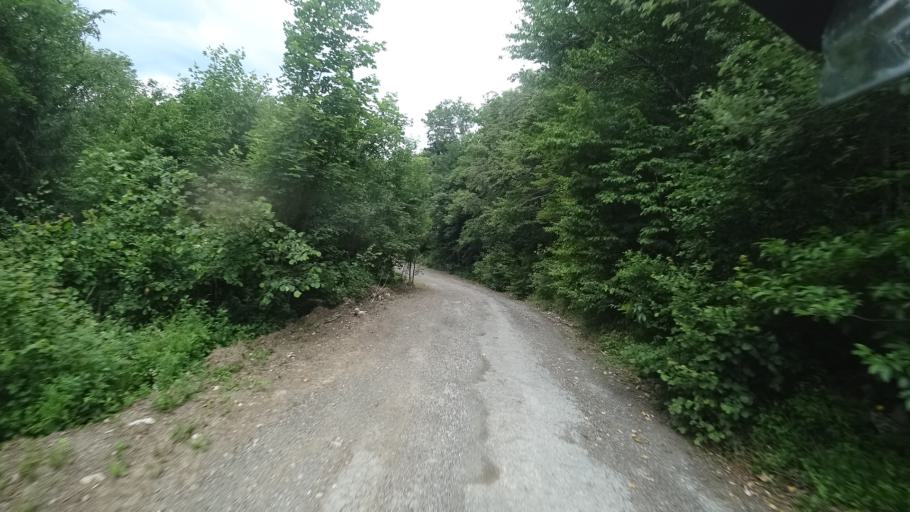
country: HR
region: Primorsko-Goranska
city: Hreljin
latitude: 45.3276
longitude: 14.7038
